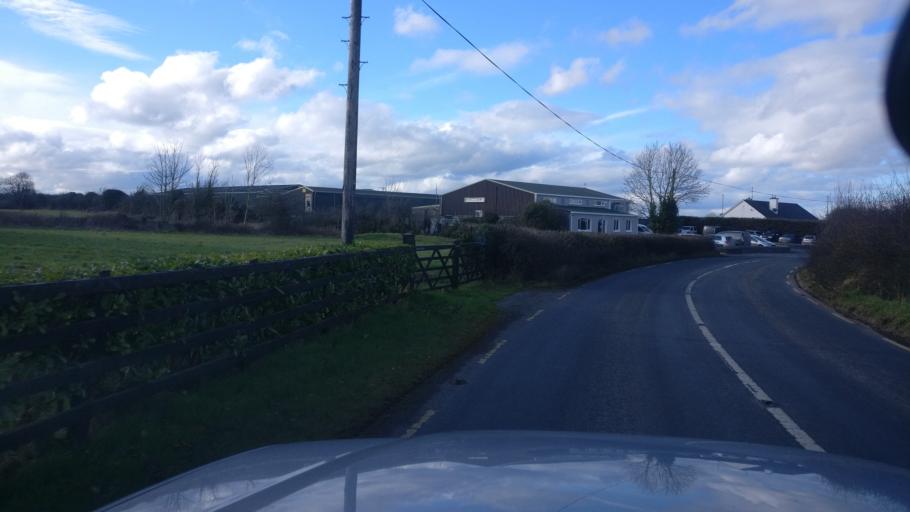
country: IE
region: Connaught
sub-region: County Galway
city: Loughrea
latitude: 53.1744
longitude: -8.3941
